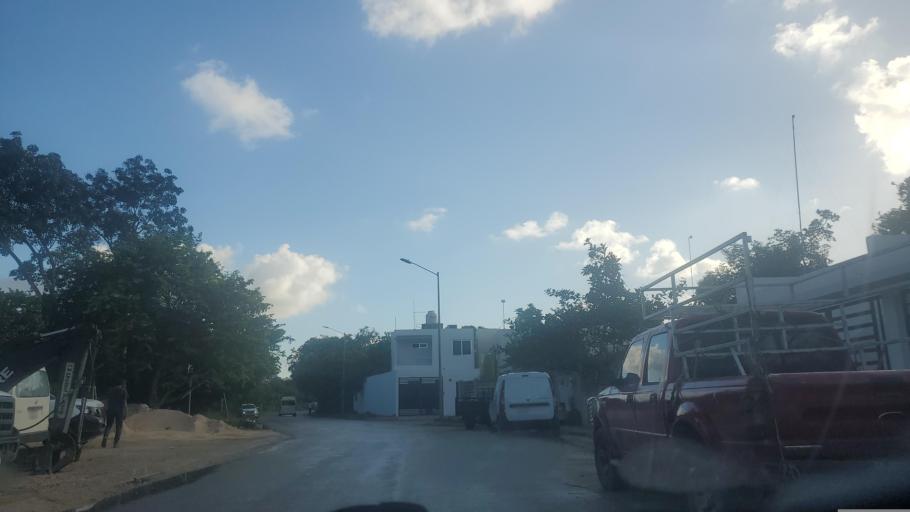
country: MX
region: Quintana Roo
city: Tulum
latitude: 20.2165
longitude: -87.4566
